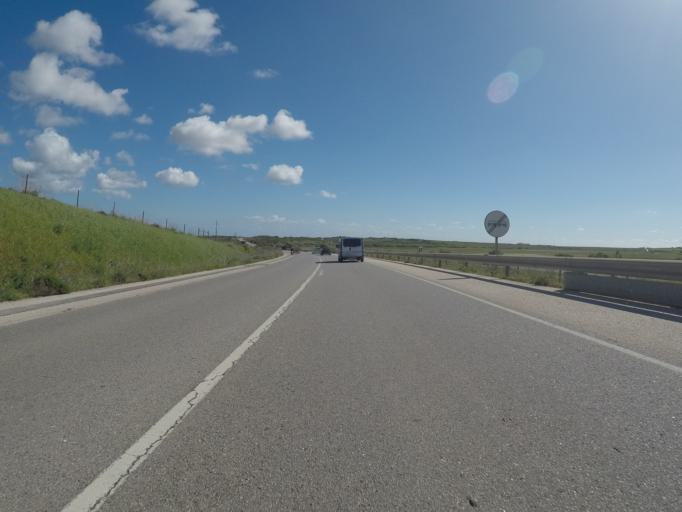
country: PT
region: Faro
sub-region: Vila do Bispo
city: Vila do Bispo
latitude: 37.0664
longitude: -8.9225
